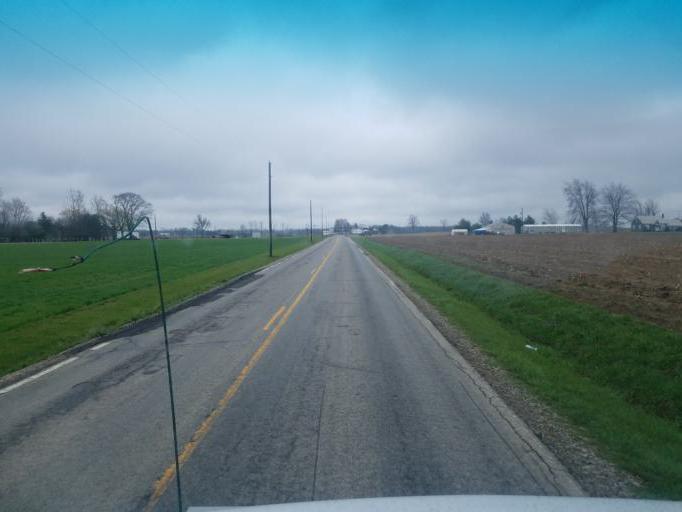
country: US
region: Ohio
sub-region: Richland County
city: Shelby
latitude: 40.9319
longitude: -82.6442
